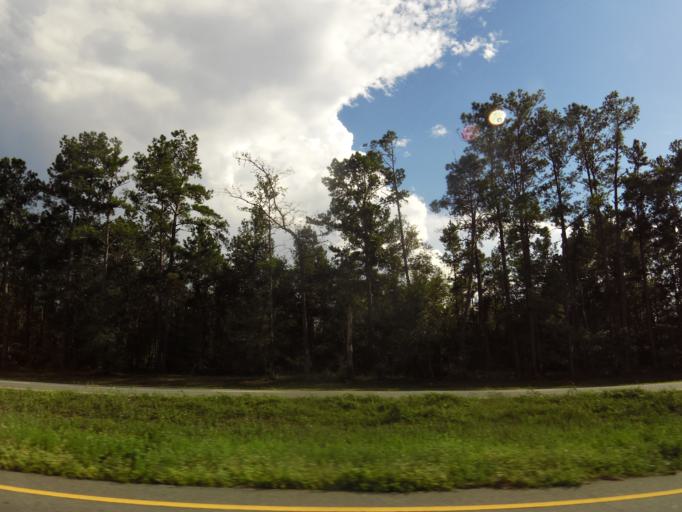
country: US
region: Georgia
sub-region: Brooks County
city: Quitman
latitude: 30.7945
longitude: -83.4405
